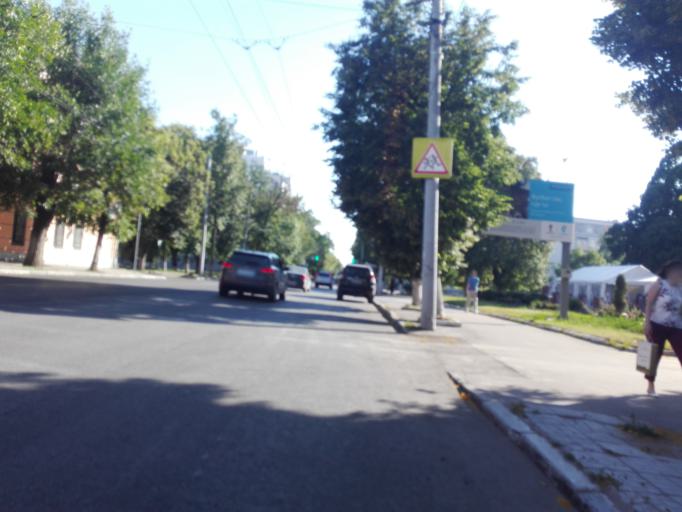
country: RU
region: Orjol
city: Orel
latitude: 52.9740
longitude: 36.0608
